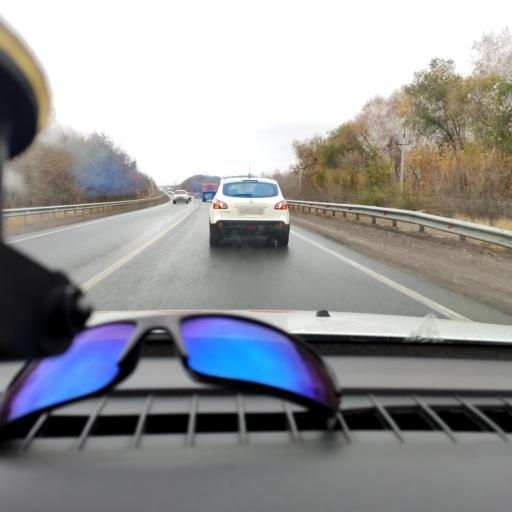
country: RU
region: Samara
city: Novokuybyshevsk
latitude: 53.0809
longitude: 50.0798
